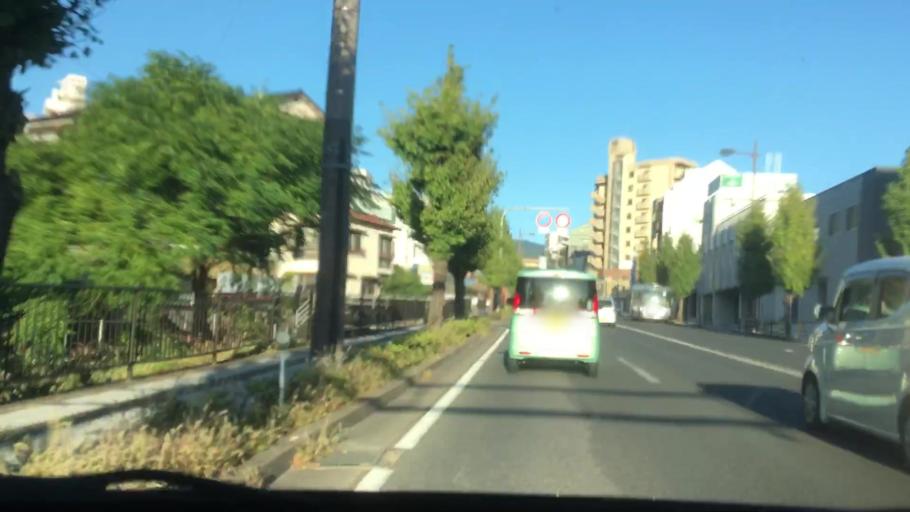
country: JP
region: Nagasaki
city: Sasebo
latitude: 33.1589
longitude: 129.7382
